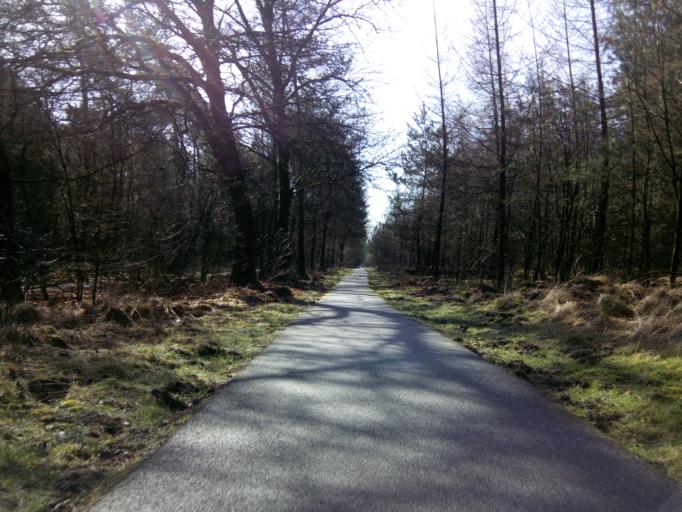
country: NL
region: Gelderland
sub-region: Gemeente Apeldoorn
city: Uddel
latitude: 52.2019
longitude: 5.8118
